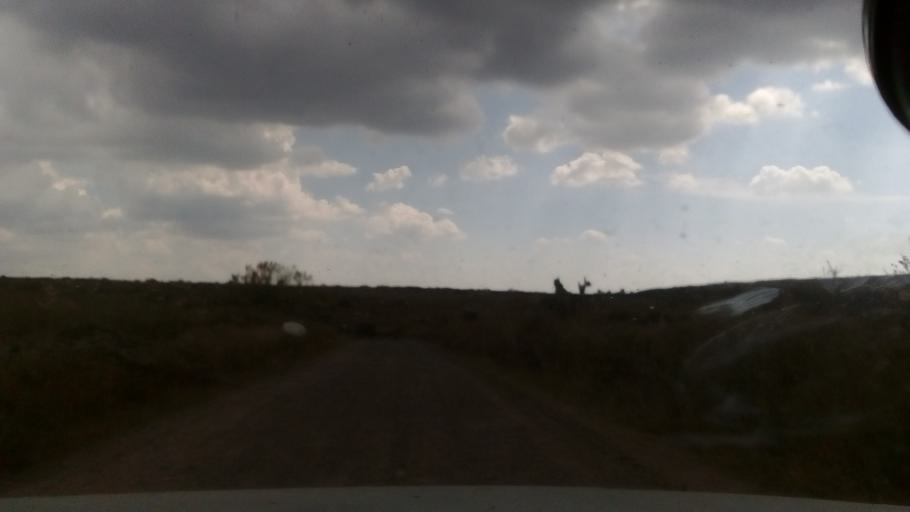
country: MX
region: Guanajuato
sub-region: Silao de la Victoria
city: San Francisco (Banos de Agua Caliente)
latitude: 21.1830
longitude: -101.4174
